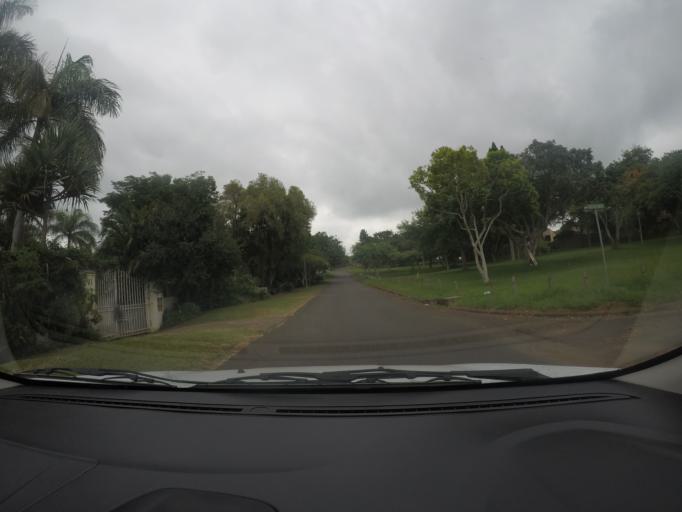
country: ZA
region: KwaZulu-Natal
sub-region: uThungulu District Municipality
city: Empangeni
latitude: -28.7635
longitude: 31.8946
